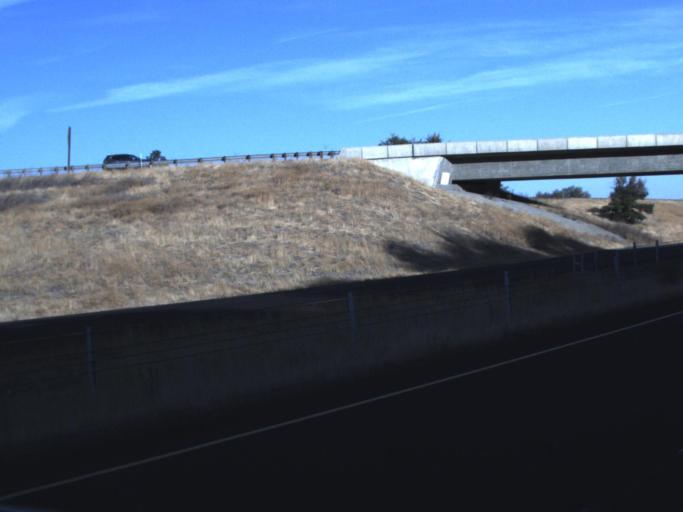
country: US
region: Washington
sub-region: Yakima County
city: Union Gap
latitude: 46.5404
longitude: -120.4708
